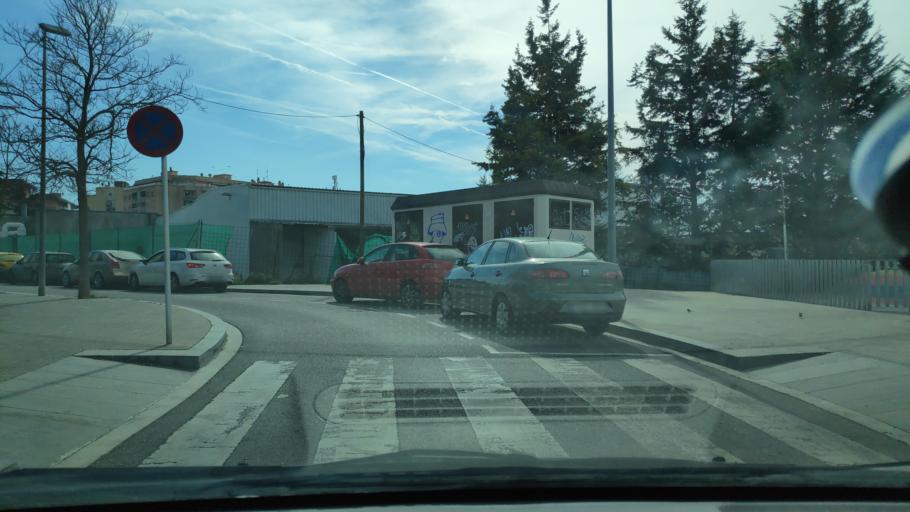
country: ES
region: Catalonia
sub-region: Provincia de Barcelona
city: Rubi
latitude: 41.4983
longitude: 2.0340
